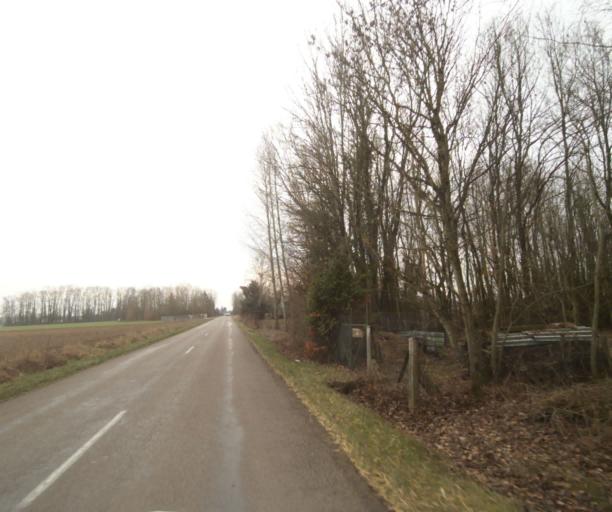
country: FR
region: Champagne-Ardenne
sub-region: Departement de la Haute-Marne
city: Villiers-en-Lieu
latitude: 48.6737
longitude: 4.8898
